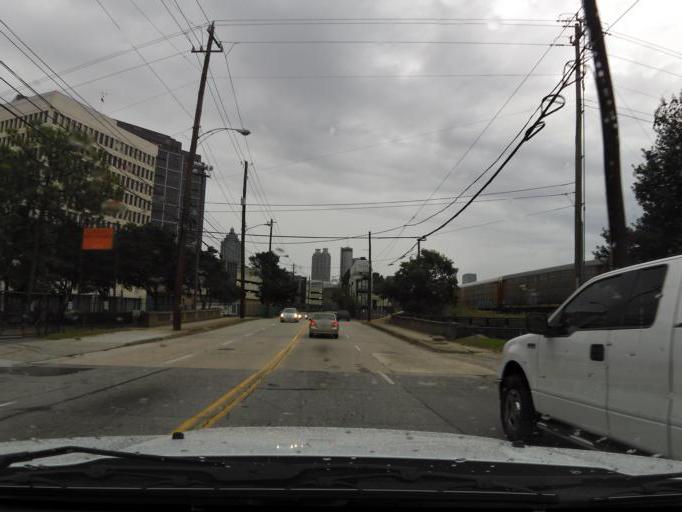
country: US
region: Georgia
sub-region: Fulton County
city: Atlanta
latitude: 33.7711
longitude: -84.4002
